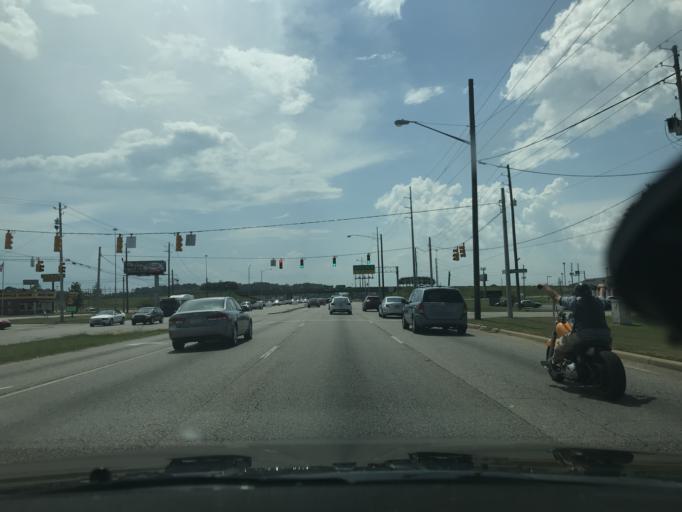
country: US
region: Alabama
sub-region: Montgomery County
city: Montgomery
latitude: 32.3821
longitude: -86.2063
